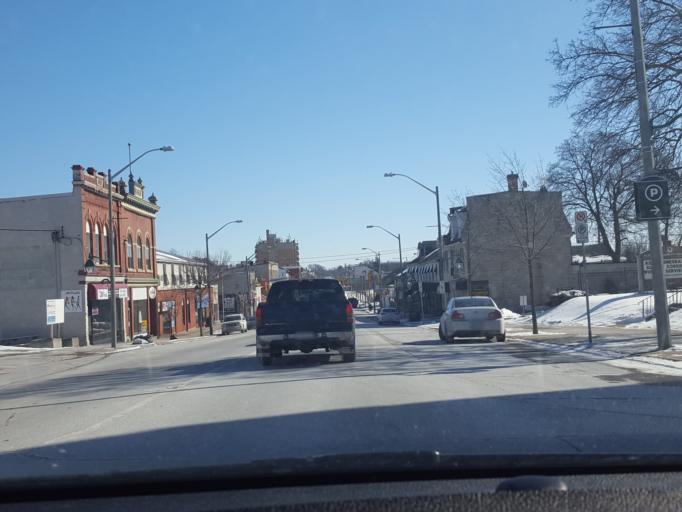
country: CA
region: Ontario
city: Cambridge
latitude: 43.3952
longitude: -80.3571
